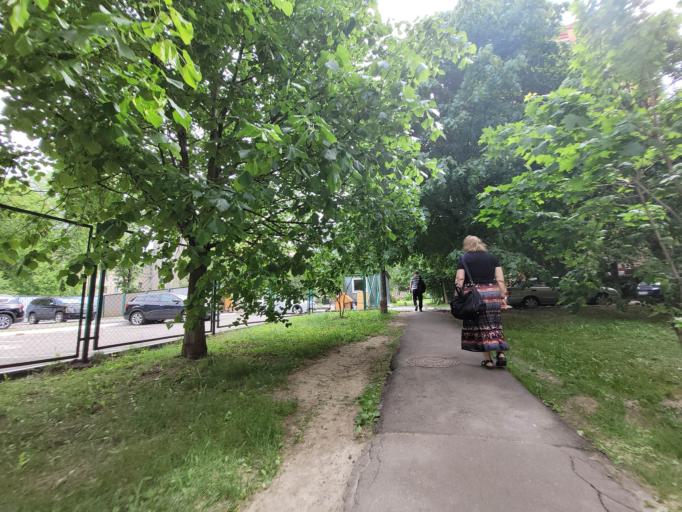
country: RU
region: Moskovskaya
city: Bolshevo
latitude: 55.9280
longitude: 37.8209
